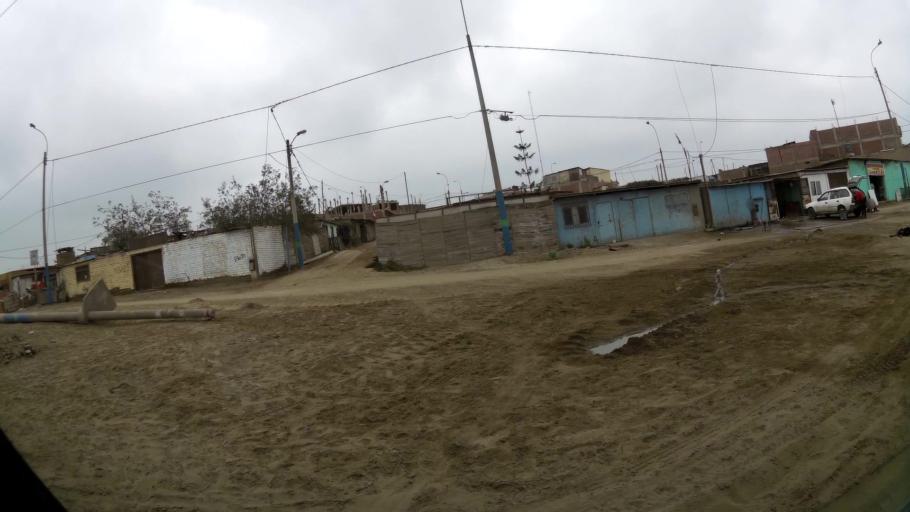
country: PE
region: Lima
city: Ventanilla
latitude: -11.8506
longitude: -77.1361
